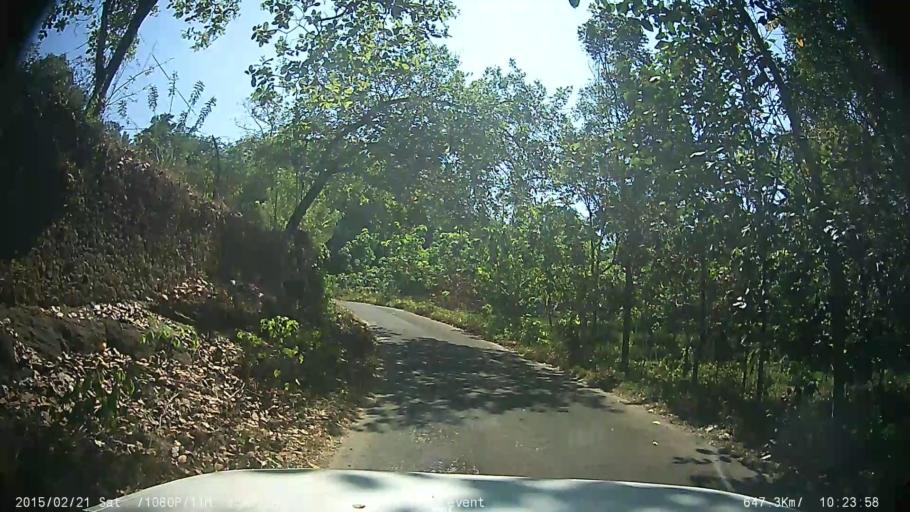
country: IN
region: Kerala
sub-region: Kottayam
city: Palackattumala
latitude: 9.8586
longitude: 76.6778
